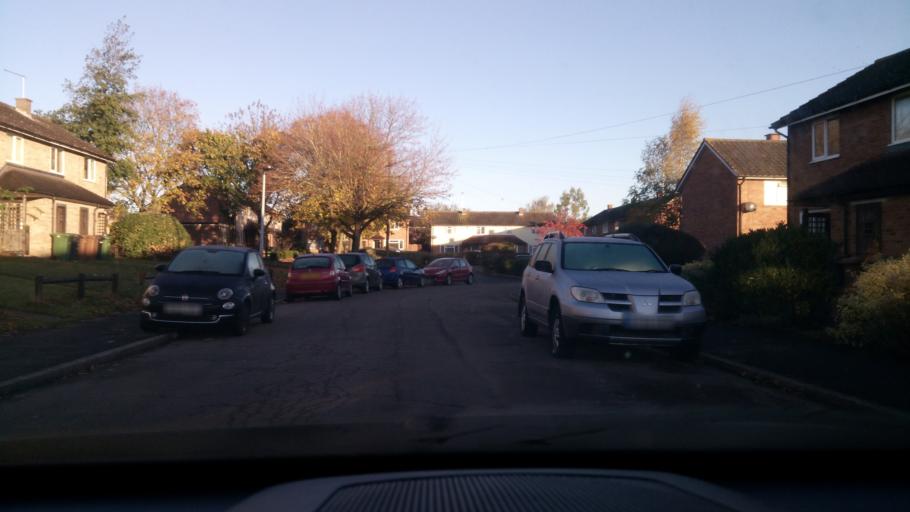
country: GB
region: England
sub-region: Peterborough
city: Wittering
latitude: 52.6072
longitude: -0.4356
